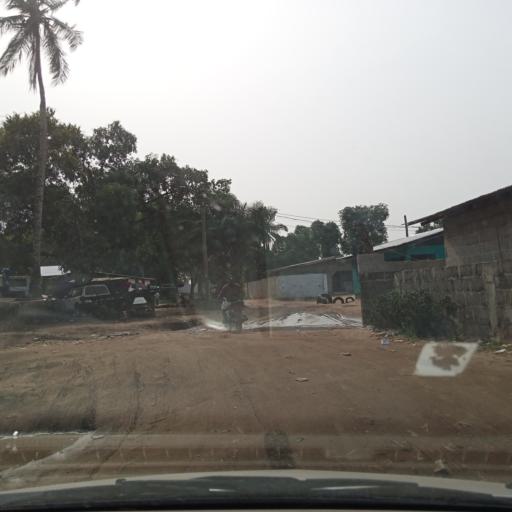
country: LR
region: Montserrado
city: Monrovia
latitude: 6.3375
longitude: -10.7466
